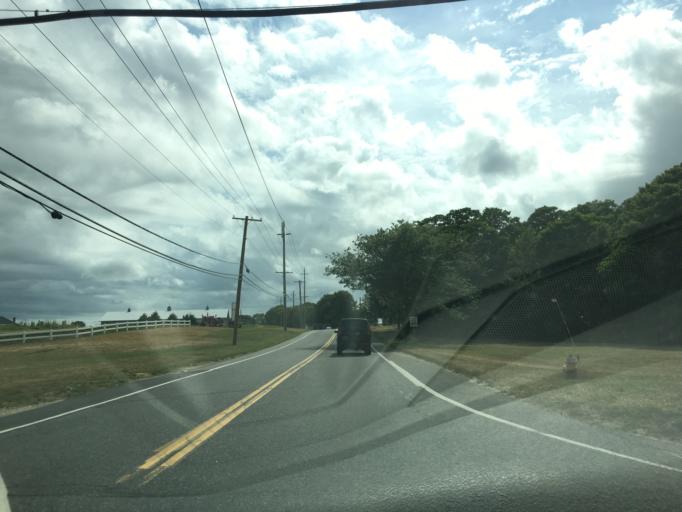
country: US
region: New York
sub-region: Suffolk County
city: Northville
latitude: 40.9776
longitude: -72.6075
